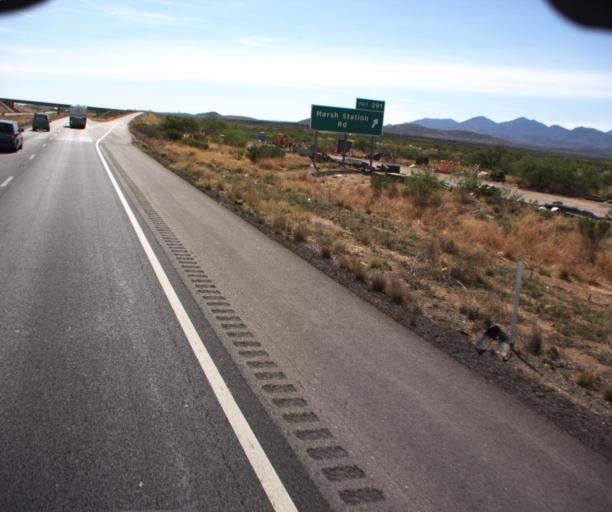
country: US
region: Arizona
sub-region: Cochise County
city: Mescal
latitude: 31.9826
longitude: -110.5425
